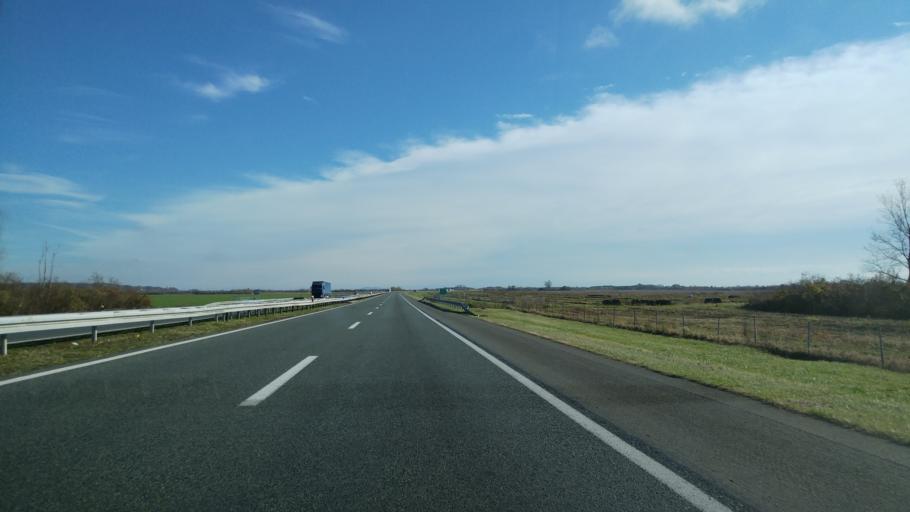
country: HR
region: Brodsko-Posavska
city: Okucani
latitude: 45.2654
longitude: 17.1519
